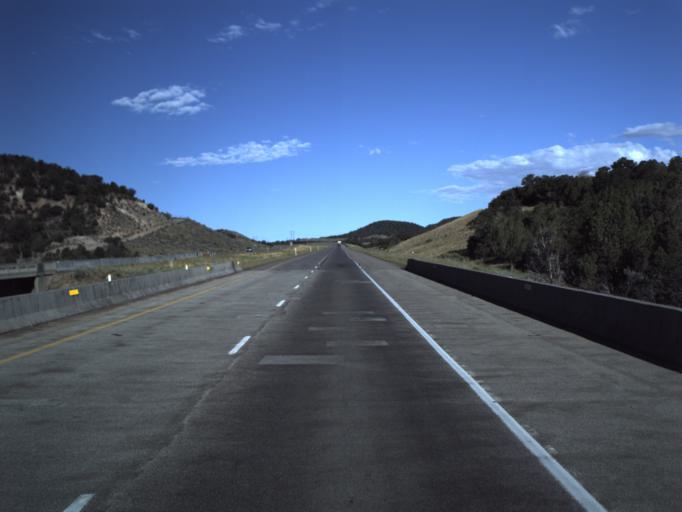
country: US
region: Utah
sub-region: Sevier County
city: Monroe
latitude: 38.5481
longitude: -112.3804
